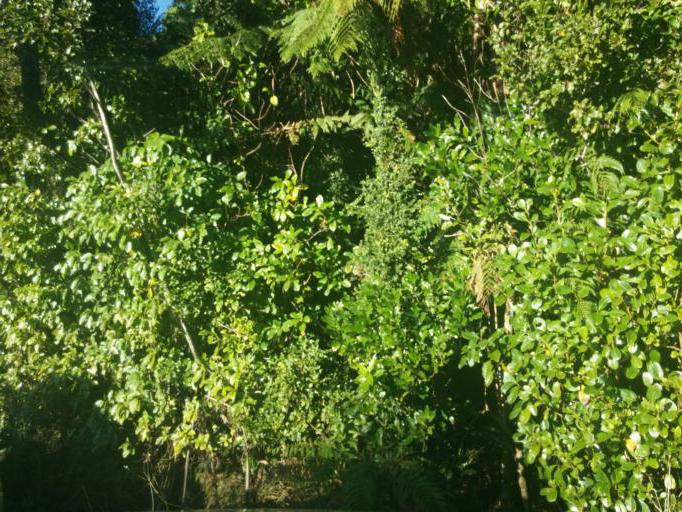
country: NZ
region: West Coast
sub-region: Grey District
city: Greymouth
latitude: -42.0961
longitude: 171.3434
